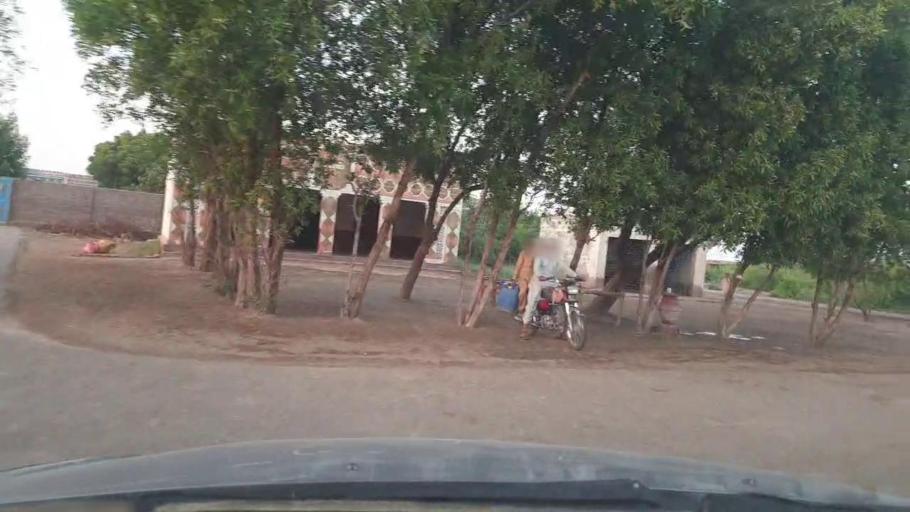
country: PK
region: Sindh
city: Tando Ghulam Ali
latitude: 25.1163
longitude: 68.9886
